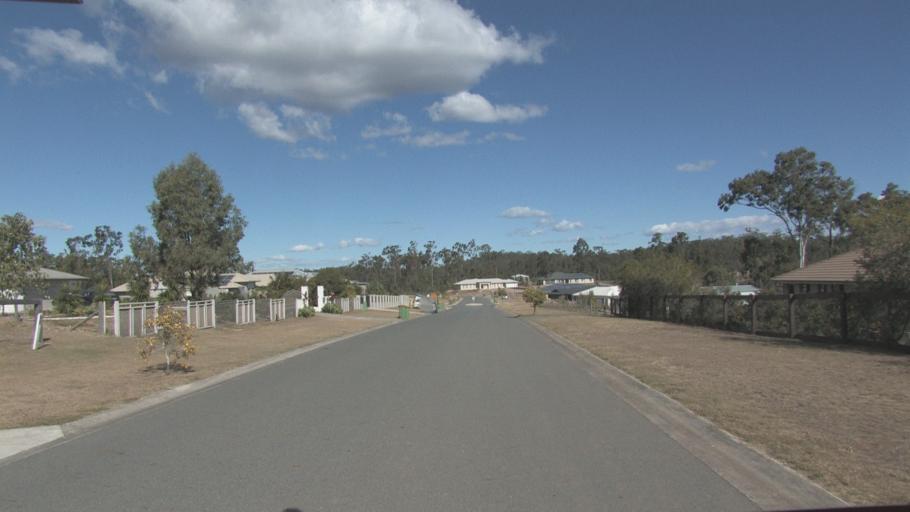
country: AU
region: Queensland
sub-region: Logan
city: North Maclean
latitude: -27.7578
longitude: 152.9347
